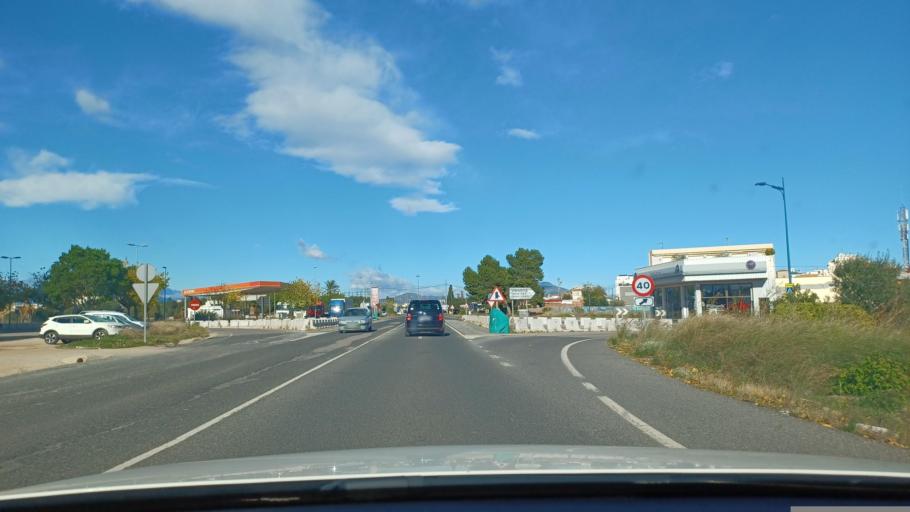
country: ES
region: Valencia
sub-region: Provincia de Castello
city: Vinaros
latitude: 40.4670
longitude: 0.4645
